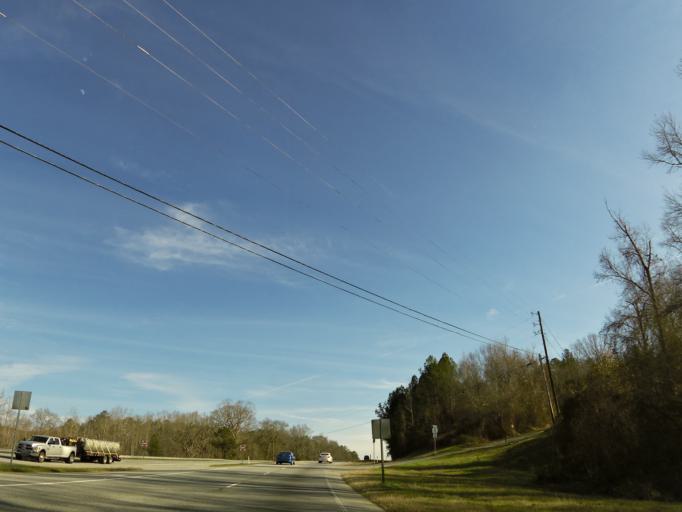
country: US
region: Georgia
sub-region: Chattahoochee County
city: Cusseta
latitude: 32.2589
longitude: -84.7272
